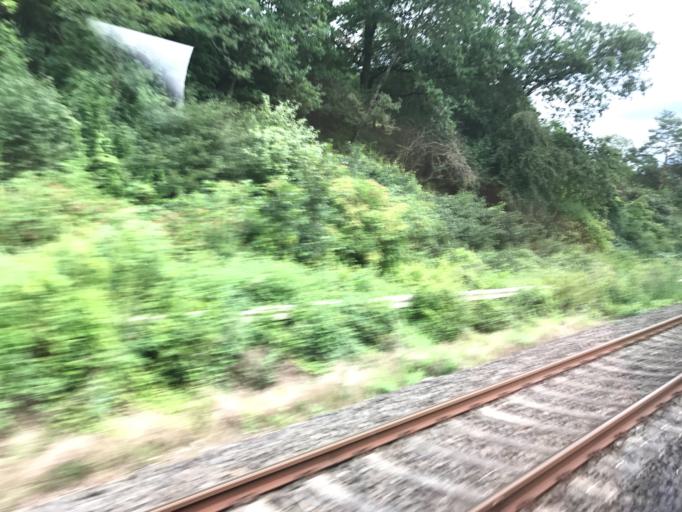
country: DE
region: Hesse
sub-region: Regierungsbezirk Giessen
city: Runkel
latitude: 50.3965
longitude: 8.1711
